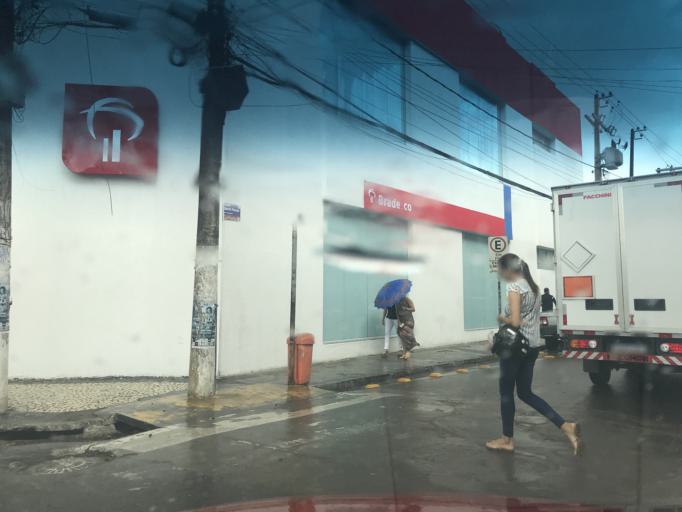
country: BR
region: Bahia
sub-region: Cruz Das Almas
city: Cruz das Almas
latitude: -12.6734
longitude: -39.1020
